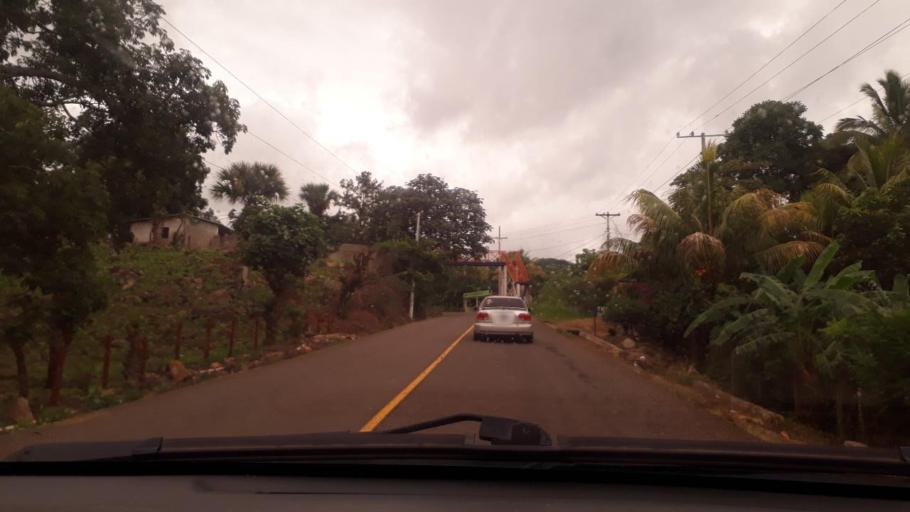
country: GT
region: Jutiapa
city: Moyuta
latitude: 13.9901
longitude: -90.0837
